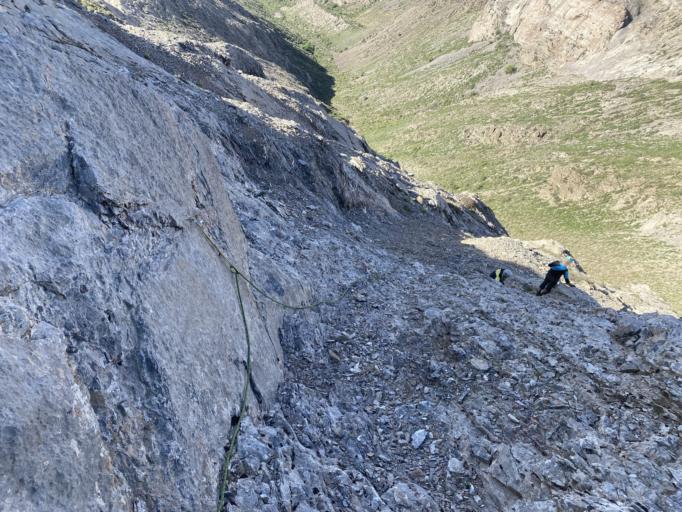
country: KZ
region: Ongtustik Qazaqstan
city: Kentau
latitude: 43.9603
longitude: 68.2463
